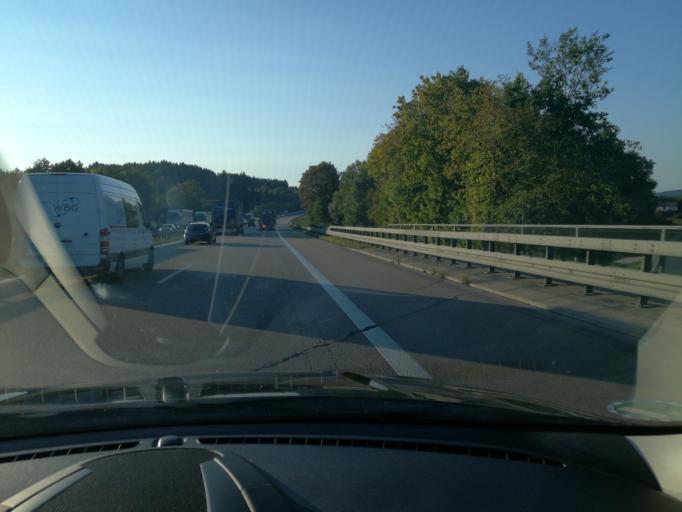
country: DE
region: Bavaria
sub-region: Upper Palatinate
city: Velburg
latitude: 49.2463
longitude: 11.6246
